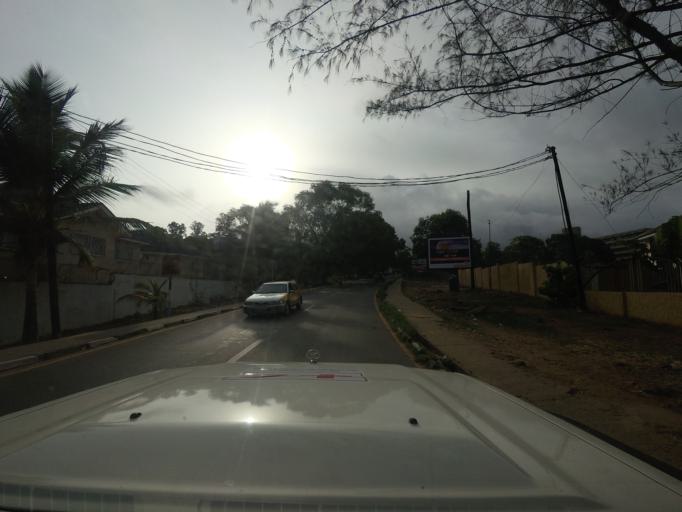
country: SL
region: Western Area
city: Freetown
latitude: 8.4936
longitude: -13.2913
